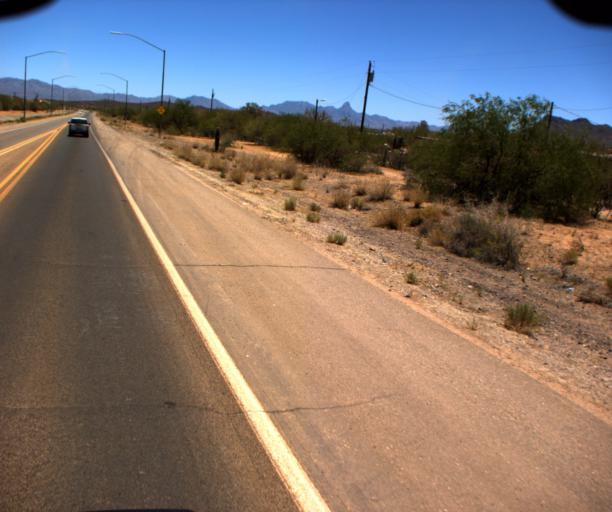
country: US
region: Arizona
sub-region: Pima County
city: Sells
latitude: 31.9172
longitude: -111.8727
